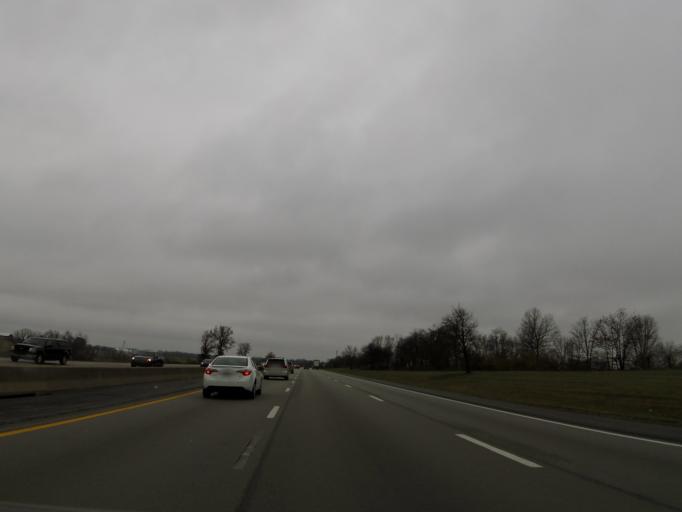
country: US
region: Kentucky
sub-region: Scott County
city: Georgetown
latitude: 38.1793
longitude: -84.5316
